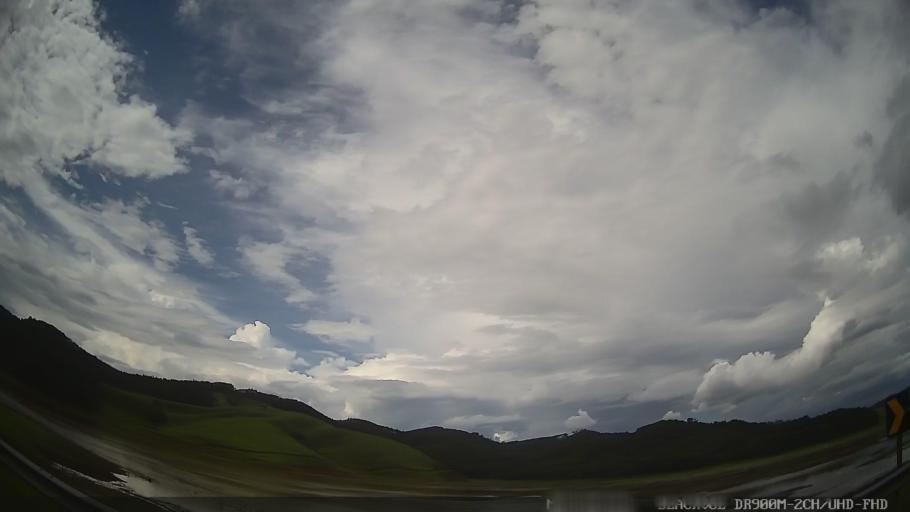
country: BR
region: Sao Paulo
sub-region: Santa Branca
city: Santa Branca
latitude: -23.5198
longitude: -45.8904
